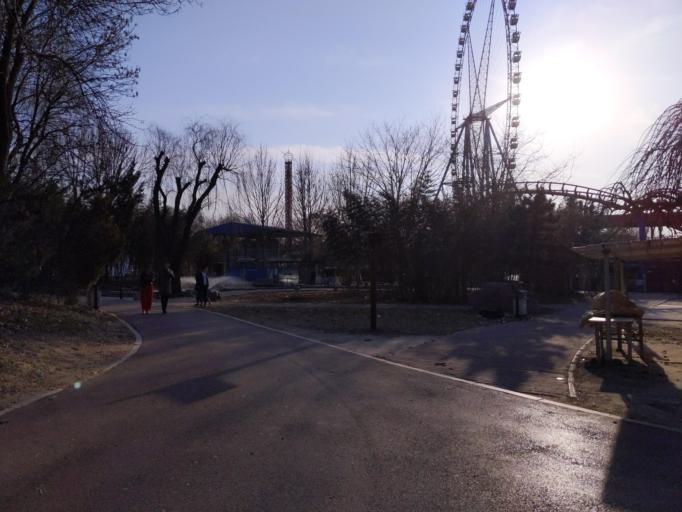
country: CN
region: Henan Sheng
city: Puyang
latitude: 35.7763
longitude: 114.9610
